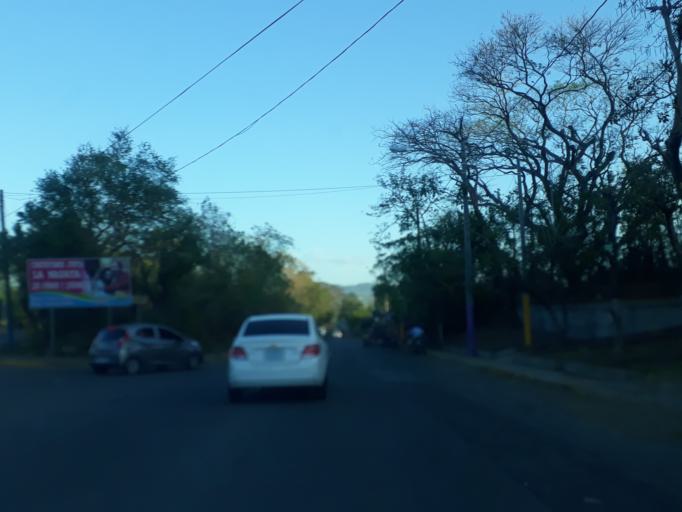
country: NI
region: Masaya
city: Nindiri
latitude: 11.9909
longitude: -86.1069
